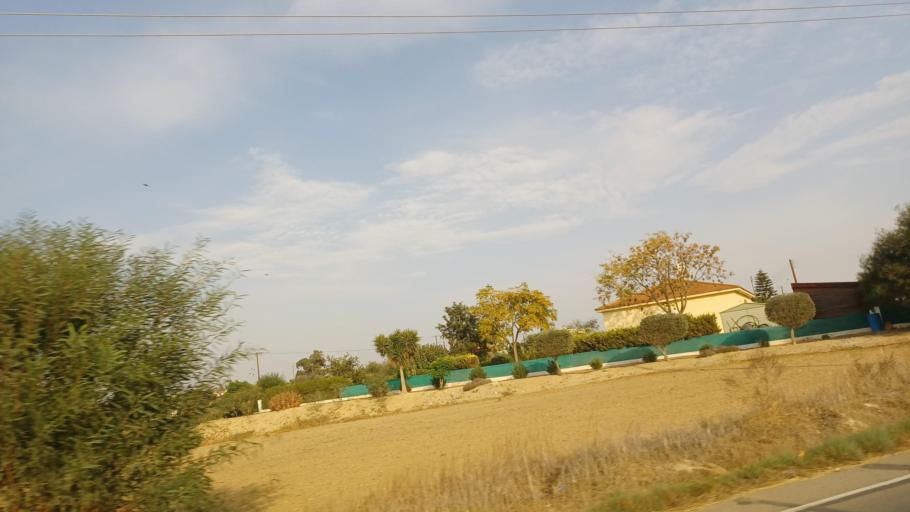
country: CY
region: Ammochostos
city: Acheritou
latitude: 35.0677
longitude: 33.8804
